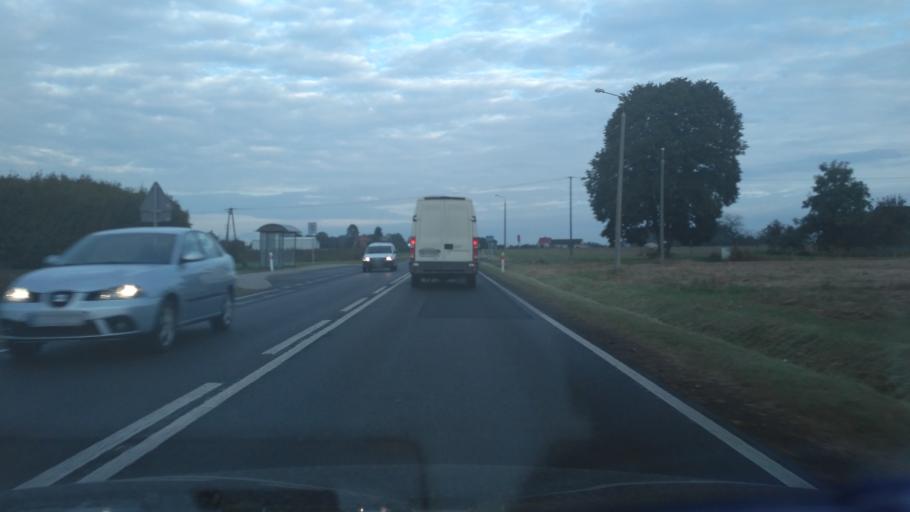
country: PL
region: Lublin Voivodeship
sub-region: Powiat leczynski
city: Spiczyn
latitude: 51.2982
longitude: 22.7697
